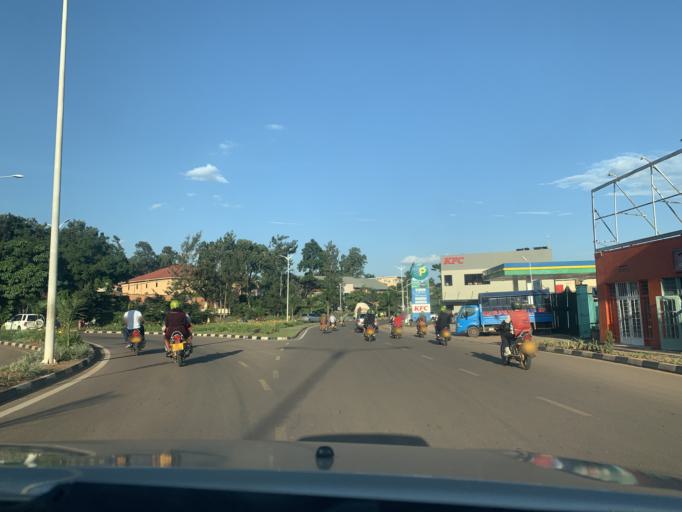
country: RW
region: Kigali
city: Kigali
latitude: -1.9598
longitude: 30.1167
